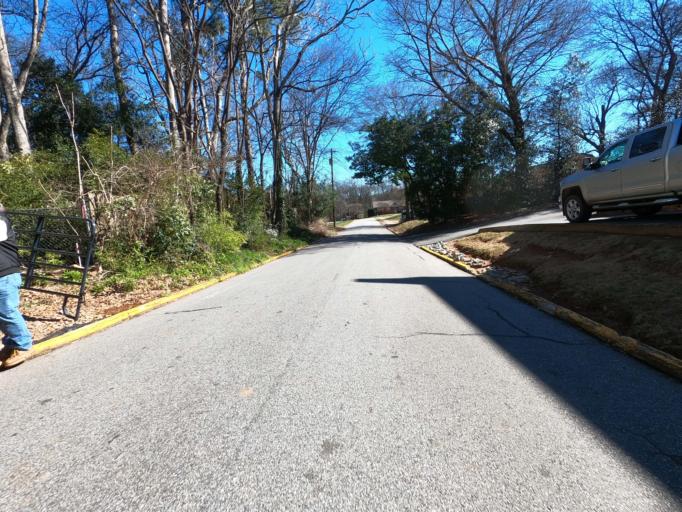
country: US
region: Georgia
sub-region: Clarke County
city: Athens
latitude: 33.9537
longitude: -83.3831
